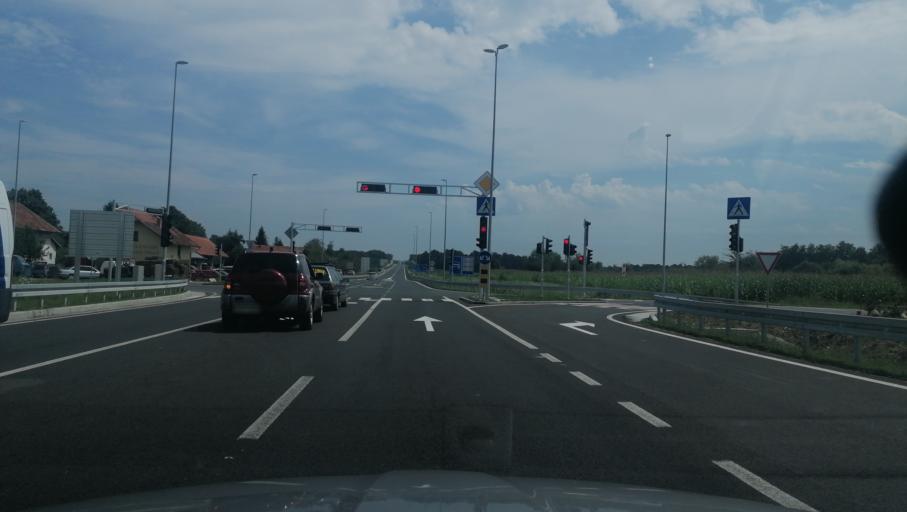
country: BA
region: Brcko
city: Brcko
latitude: 44.8352
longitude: 18.7853
